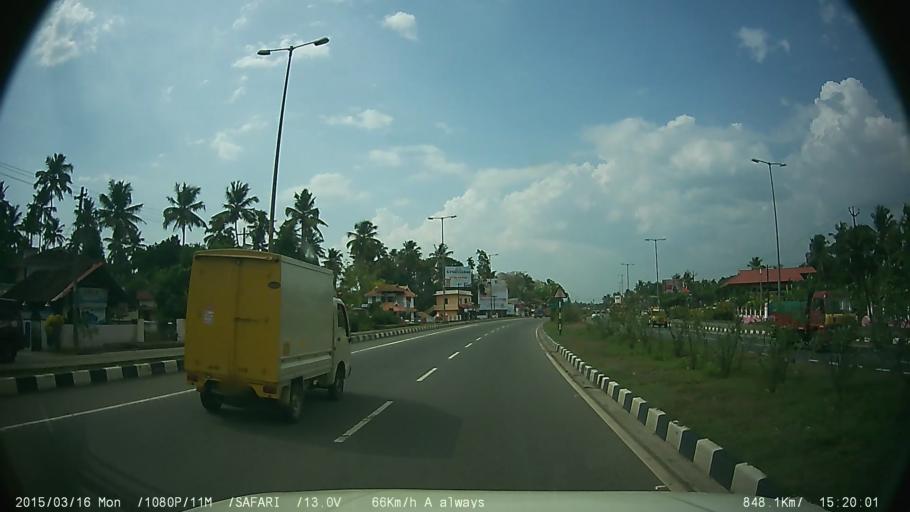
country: IN
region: Kerala
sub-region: Thrissur District
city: Kizhake Chalakudi
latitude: 10.3510
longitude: 76.3183
